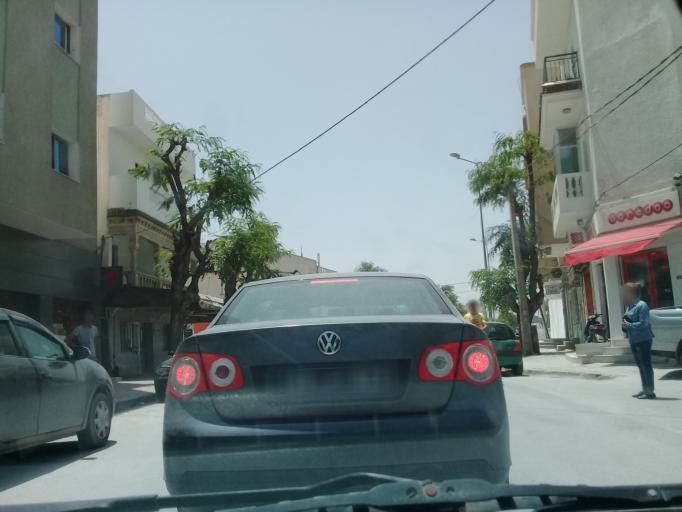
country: TN
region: Ariana
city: Ariana
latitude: 36.8301
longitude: 10.1937
